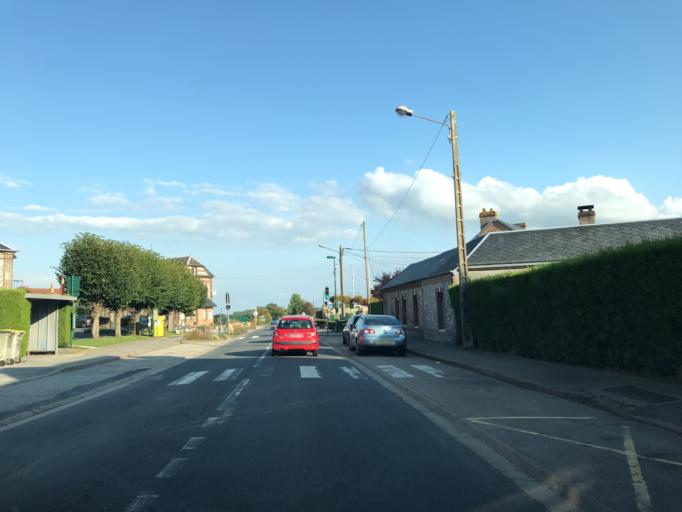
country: FR
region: Haute-Normandie
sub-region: Departement de la Seine-Maritime
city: Beuzeville-la-Grenier
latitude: 49.5913
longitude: 0.4273
